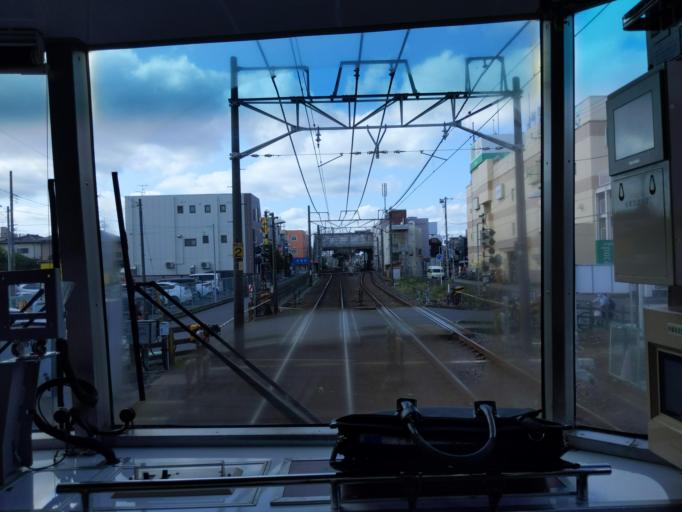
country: JP
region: Chiba
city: Funabashi
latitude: 35.7292
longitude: 140.0310
